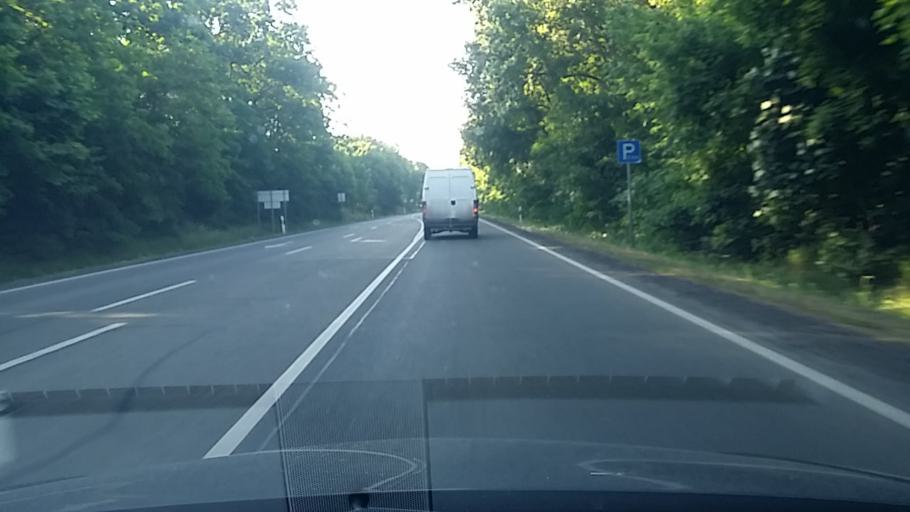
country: HU
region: Fejer
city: dunaujvaros
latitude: 46.9385
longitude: 18.9206
